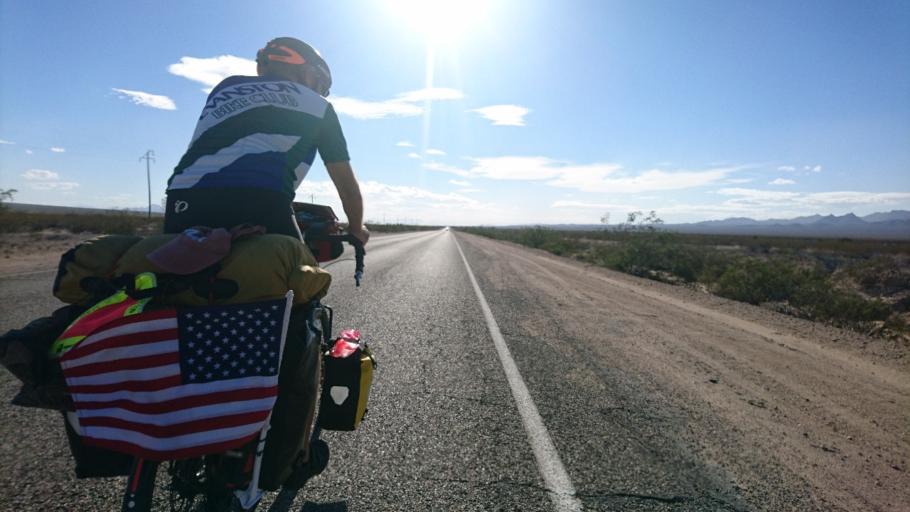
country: US
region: California
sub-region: San Bernardino County
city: Needles
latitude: 34.7224
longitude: -115.2669
